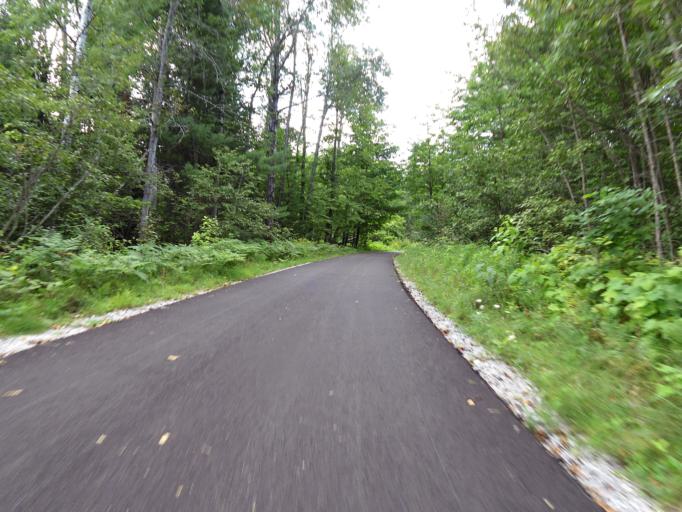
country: CA
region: Quebec
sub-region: Outaouais
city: Maniwaki
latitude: 46.1937
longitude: -76.0485
